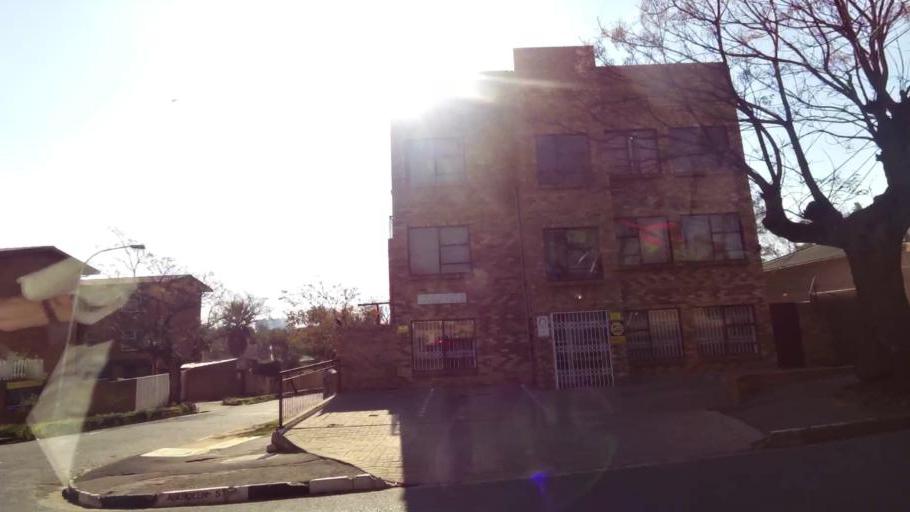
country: ZA
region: Gauteng
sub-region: City of Johannesburg Metropolitan Municipality
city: Johannesburg
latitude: -26.1804
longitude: 27.9949
